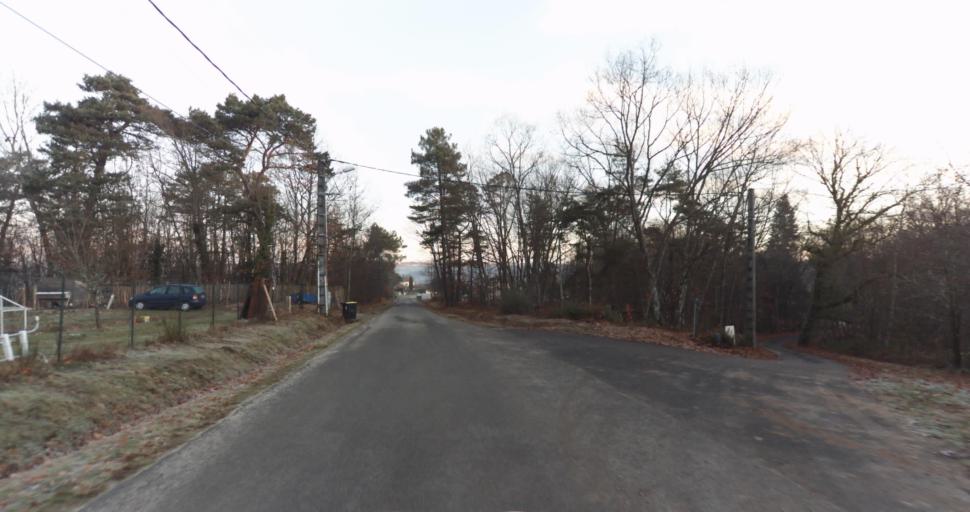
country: FR
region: Limousin
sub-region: Departement de la Haute-Vienne
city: Aixe-sur-Vienne
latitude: 45.8165
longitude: 1.1613
